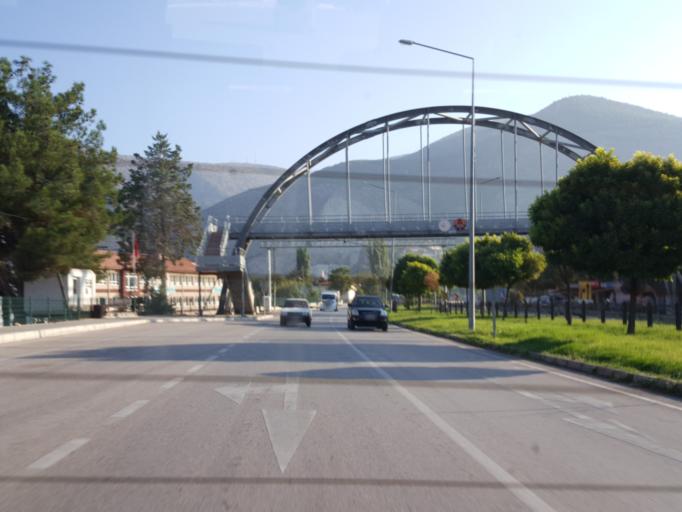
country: TR
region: Amasya
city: Amasya
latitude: 40.6175
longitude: 35.8150
